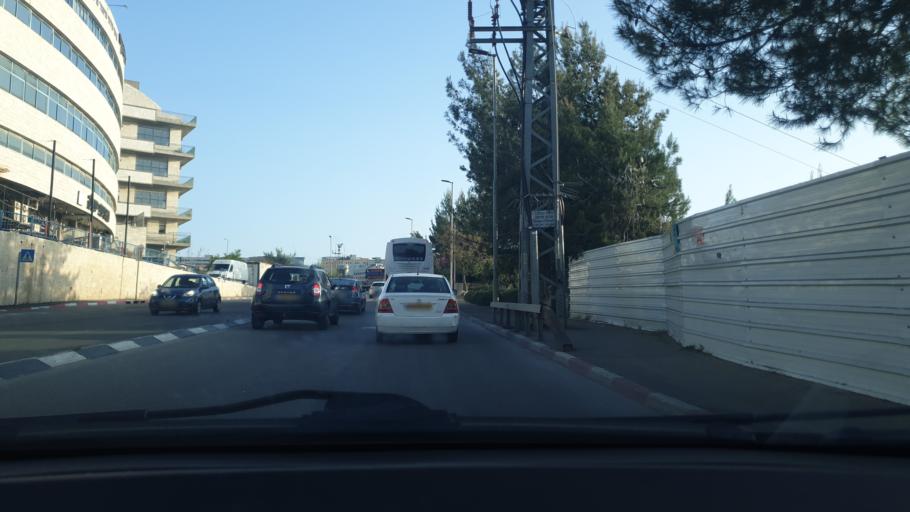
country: PS
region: West Bank
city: Bayt Iksa
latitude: 31.7949
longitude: 35.1870
